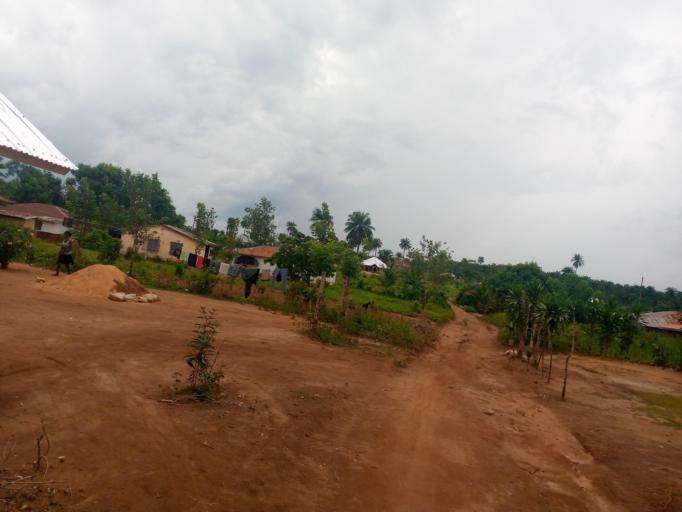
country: SL
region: Southern Province
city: Sumbuya
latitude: 7.6006
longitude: -12.1620
